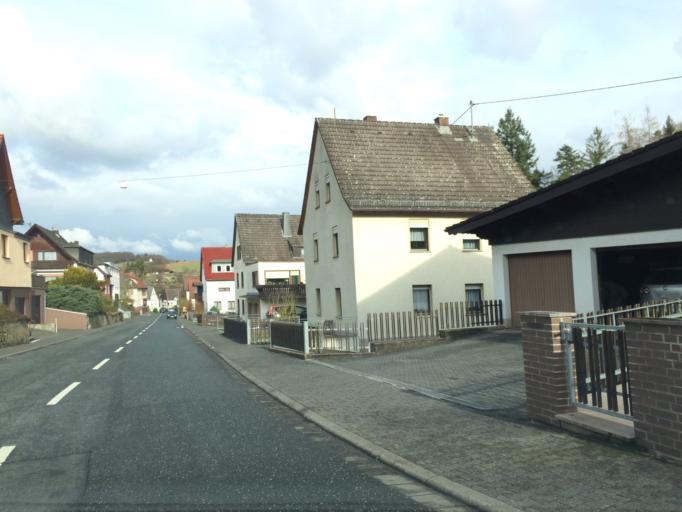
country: DE
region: Hesse
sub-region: Regierungsbezirk Darmstadt
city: Gravenwiesbach
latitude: 50.3558
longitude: 8.4047
